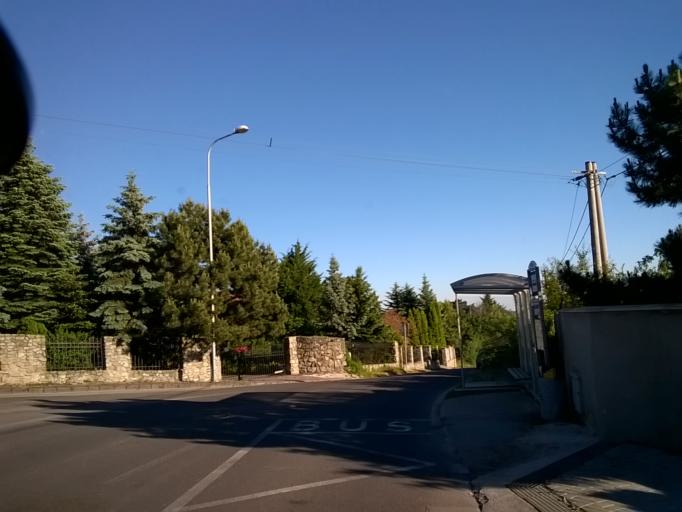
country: SK
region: Nitriansky
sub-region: Okres Nitra
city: Nitra
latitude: 48.3360
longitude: 18.0898
